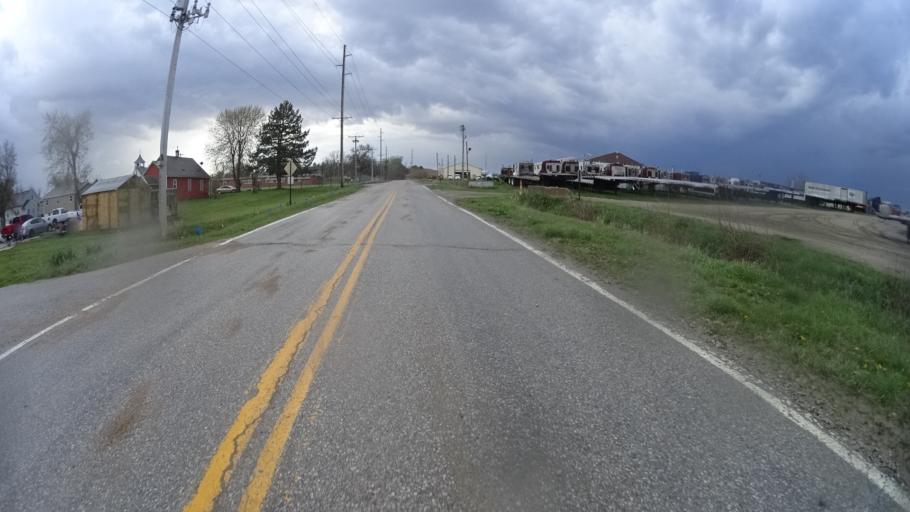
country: US
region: Nebraska
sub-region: Sarpy County
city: Offutt Air Force Base
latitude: 41.0748
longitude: -95.9230
